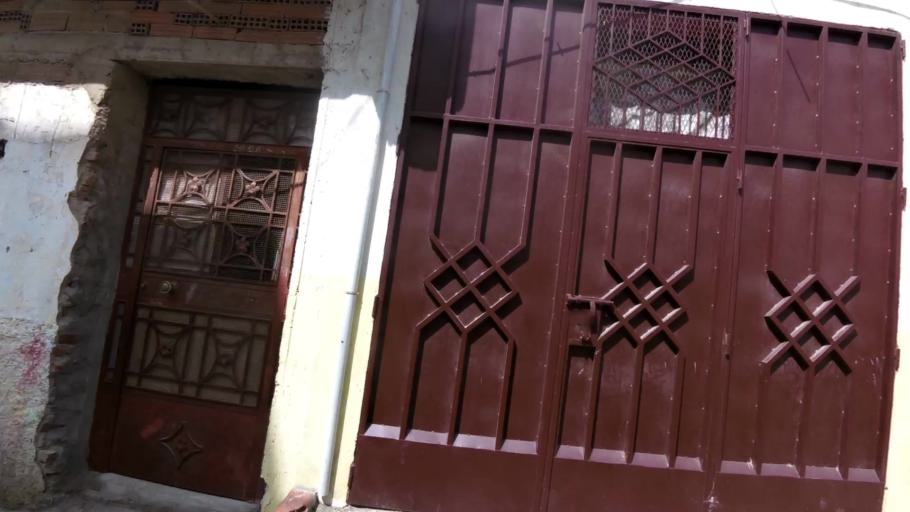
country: MA
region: Tanger-Tetouan
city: Tetouan
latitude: 35.5779
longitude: -5.3876
